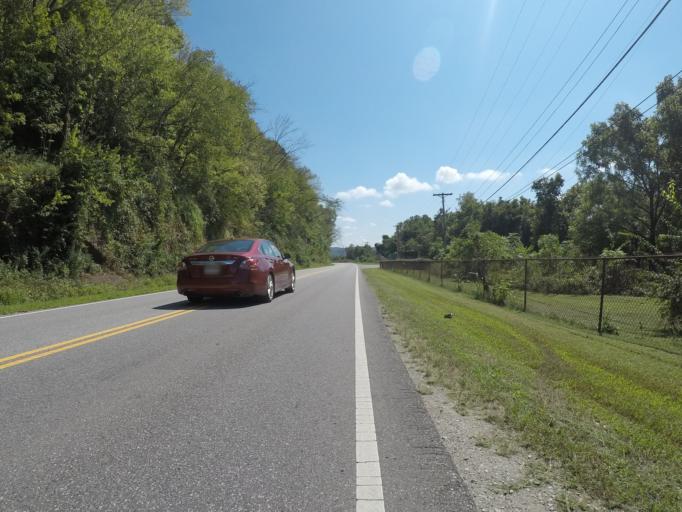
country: US
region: West Virginia
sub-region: Wayne County
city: Kenova
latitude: 38.4079
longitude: -82.5711
